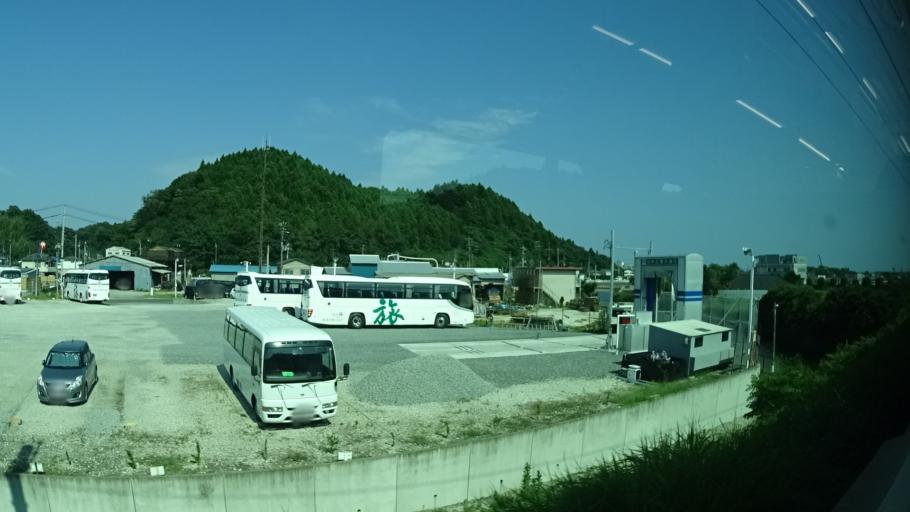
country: JP
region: Miyagi
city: Matsushima
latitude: 38.3941
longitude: 141.0649
